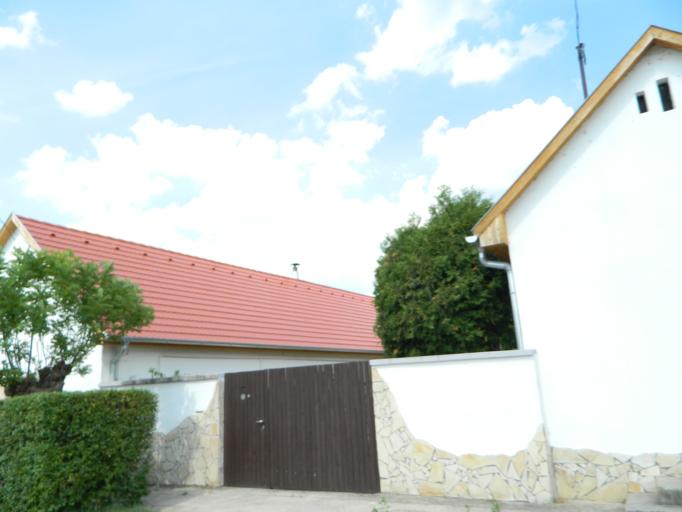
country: HU
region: Somogy
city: Balatonfoldvar
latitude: 46.8290
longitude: 17.9019
